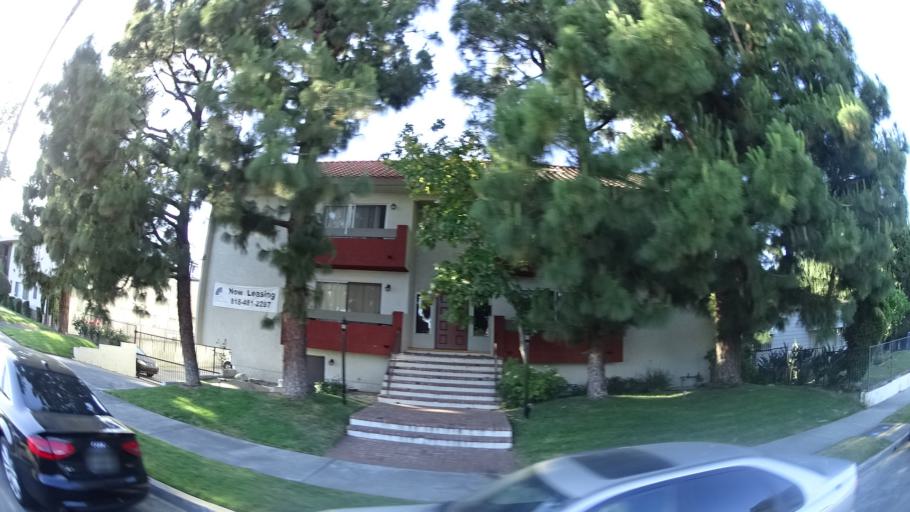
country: US
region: California
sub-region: Los Angeles County
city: North Hollywood
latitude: 34.1608
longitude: -118.3667
